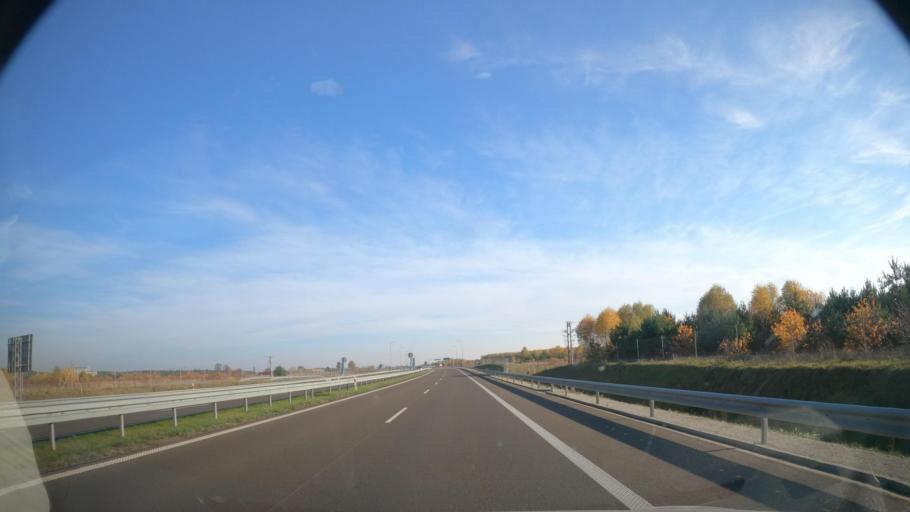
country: PL
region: West Pomeranian Voivodeship
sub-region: Powiat walecki
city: Walcz
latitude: 53.2954
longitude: 16.4458
